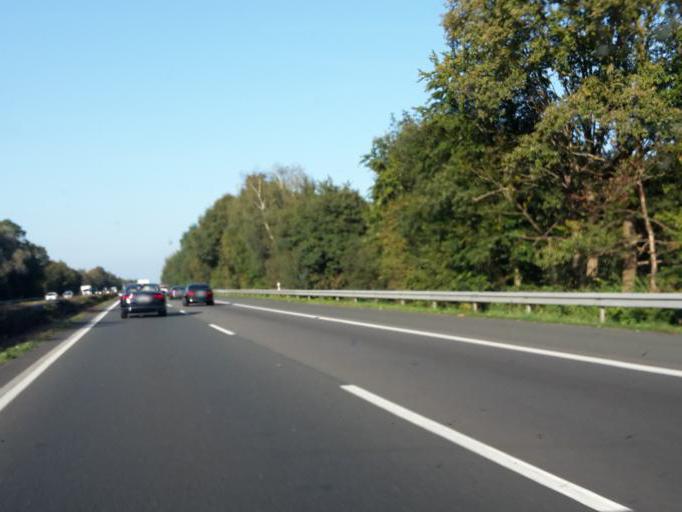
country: DE
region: North Rhine-Westphalia
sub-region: Regierungsbezirk Munster
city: Greven
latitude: 52.0389
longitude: 7.6067
